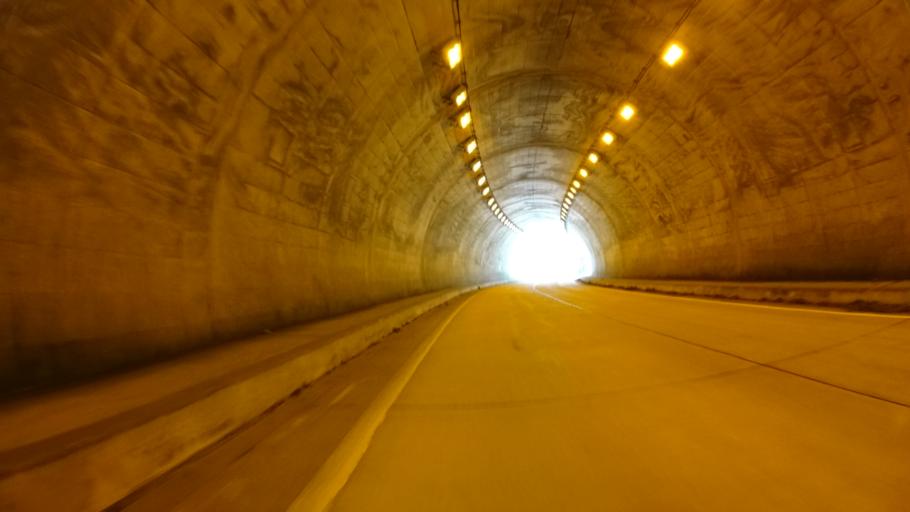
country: JP
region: Yamanashi
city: Enzan
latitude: 35.6570
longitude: 138.8166
